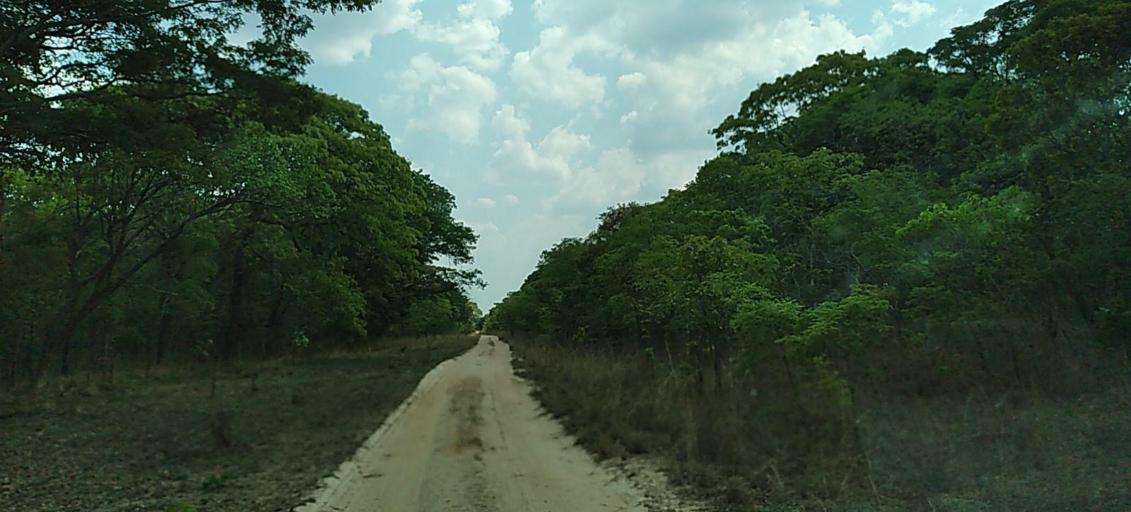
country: ZM
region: Copperbelt
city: Mpongwe
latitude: -13.8504
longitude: 27.9316
